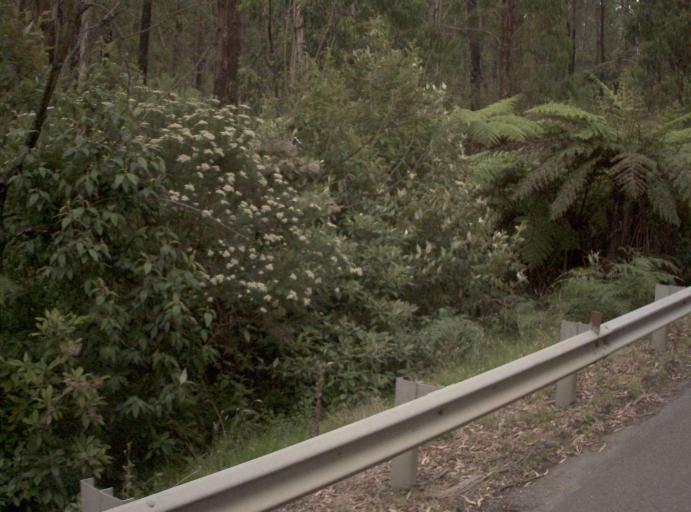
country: AU
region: Victoria
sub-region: Yarra Ranges
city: Yarra Glen
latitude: -37.5283
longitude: 145.4158
